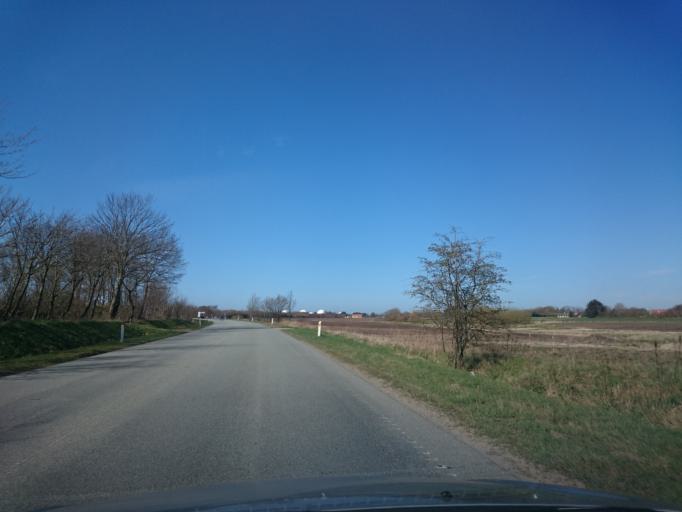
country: DK
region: North Denmark
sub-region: Hjorring Kommune
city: Hjorring
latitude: 57.4732
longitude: 10.0163
